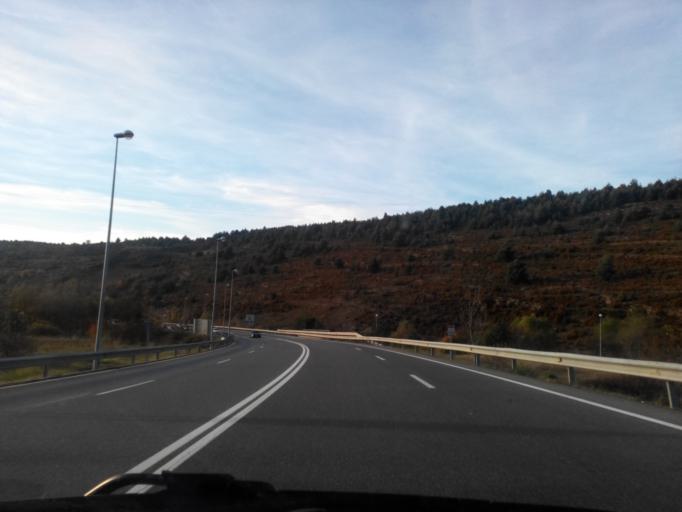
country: ES
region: Catalonia
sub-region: Provincia de Lleida
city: Riu de Cerdanya
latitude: 42.3482
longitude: 1.8322
